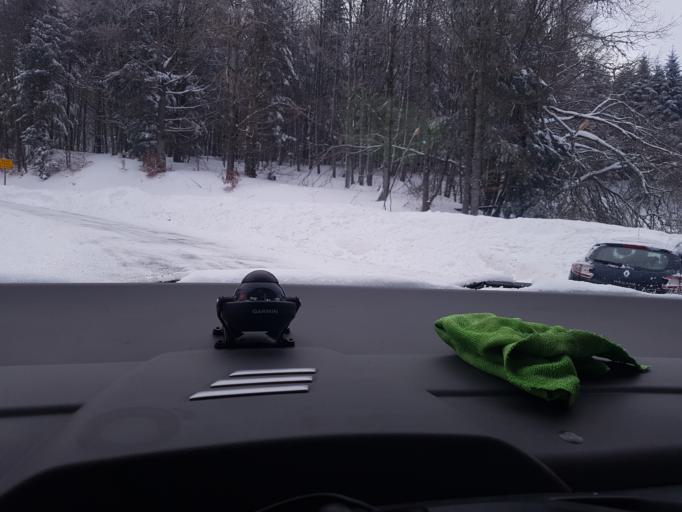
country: FR
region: Alsace
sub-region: Departement du Bas-Rhin
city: Ville
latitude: 48.3837
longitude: 7.2576
